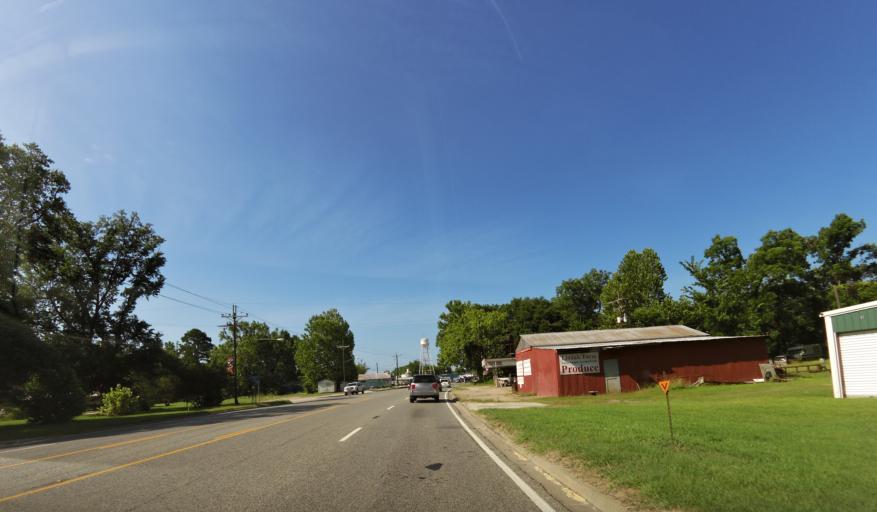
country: US
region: Texas
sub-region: Polk County
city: Corrigan
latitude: 31.0019
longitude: -94.8255
